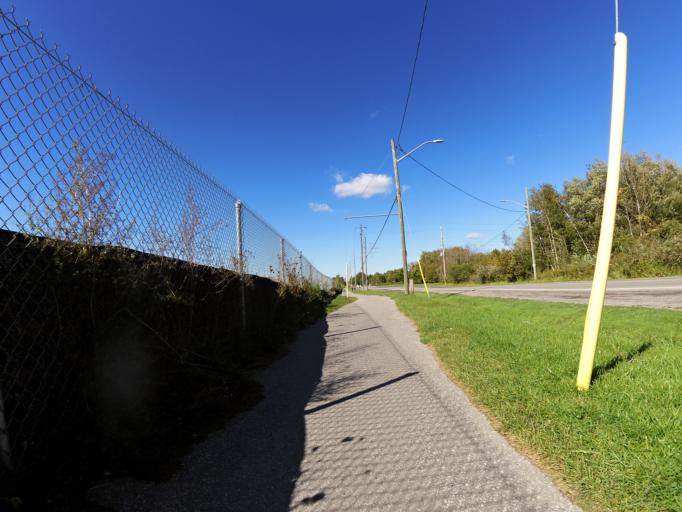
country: CA
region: Ontario
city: Oshawa
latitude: 43.8540
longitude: -78.9313
